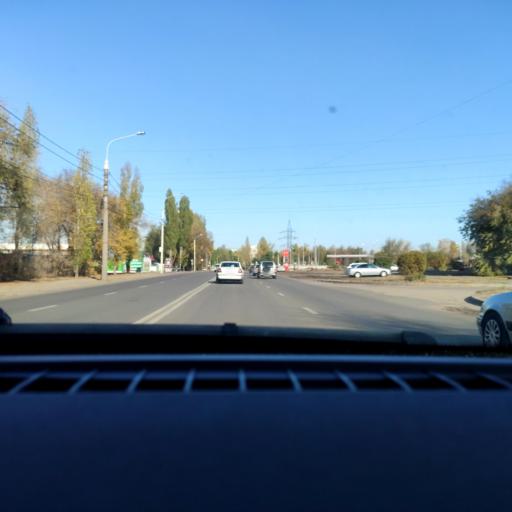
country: RU
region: Voronezj
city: Voronezh
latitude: 51.6448
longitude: 39.2673
